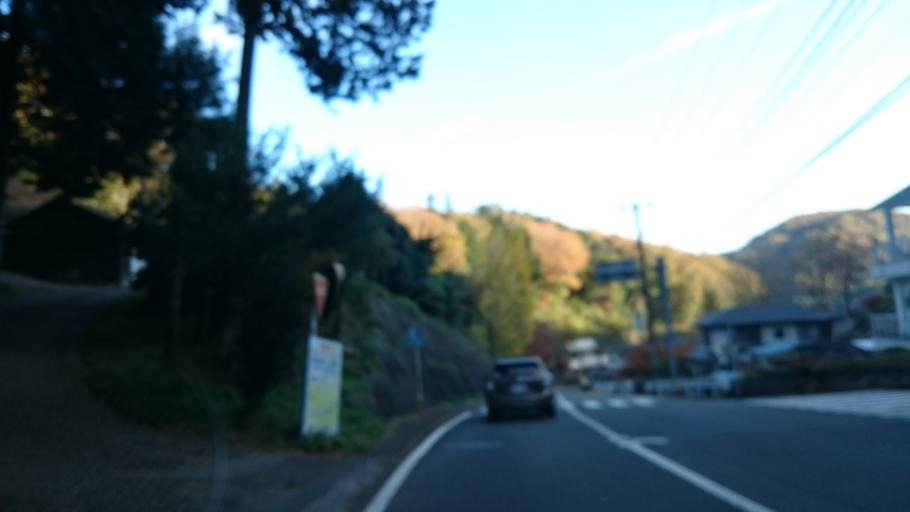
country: JP
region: Shizuoka
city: Numazu
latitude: 34.9759
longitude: 138.9272
